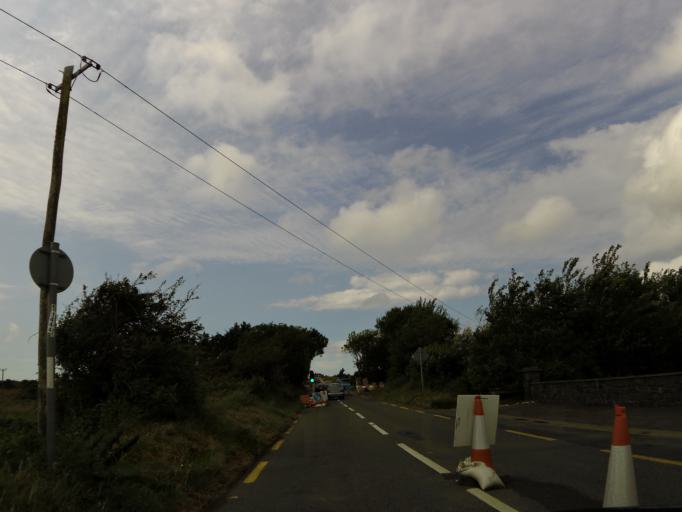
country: IE
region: Munster
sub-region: An Clar
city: Kilrush
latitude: 52.6751
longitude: -9.6142
